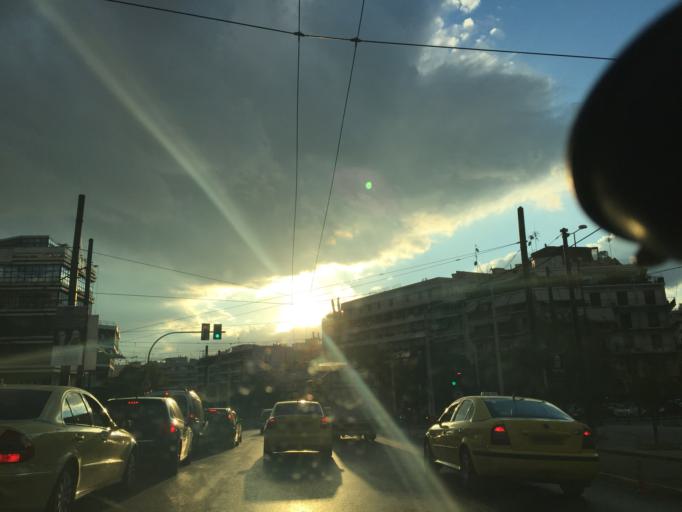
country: GR
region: Attica
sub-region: Nomarchia Athinas
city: Dhafni
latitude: 37.9673
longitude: 23.7340
